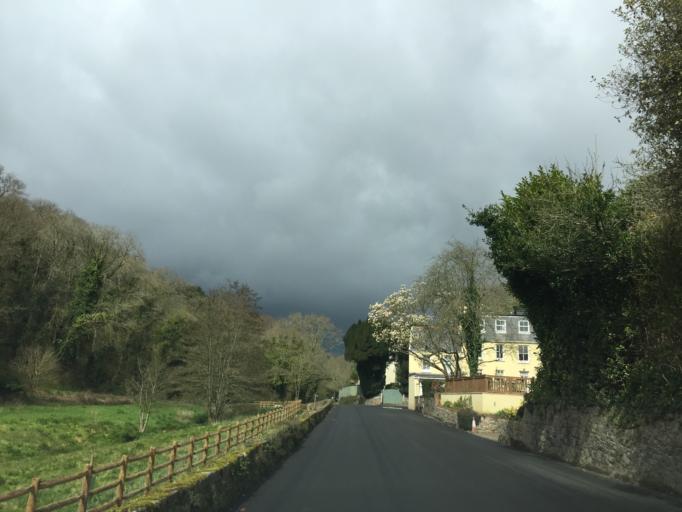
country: JE
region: St Helier
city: Saint Helier
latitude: 49.2143
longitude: -2.1709
